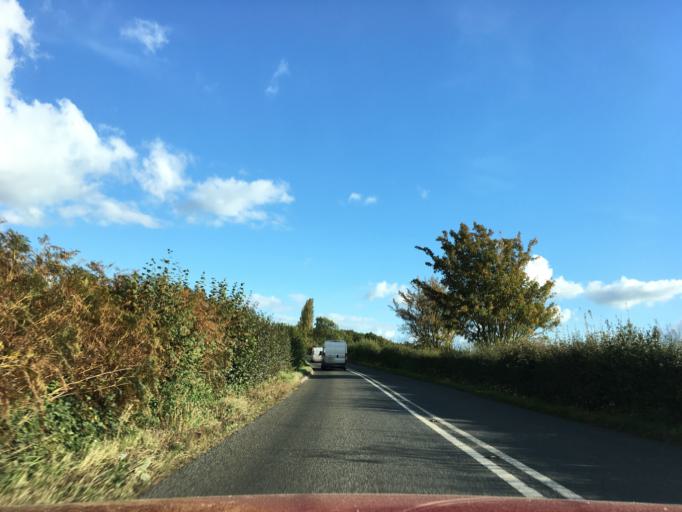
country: GB
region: England
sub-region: Herefordshire
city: Kinnersley
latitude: 52.1048
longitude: -2.9550
